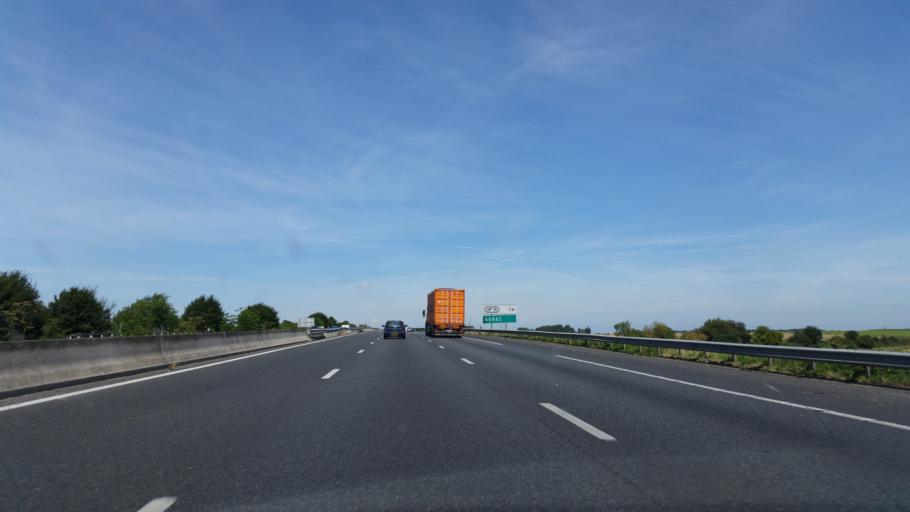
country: FR
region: Nord-Pas-de-Calais
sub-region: Departement du Pas-de-Calais
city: Bapaume
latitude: 50.1115
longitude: 2.8717
